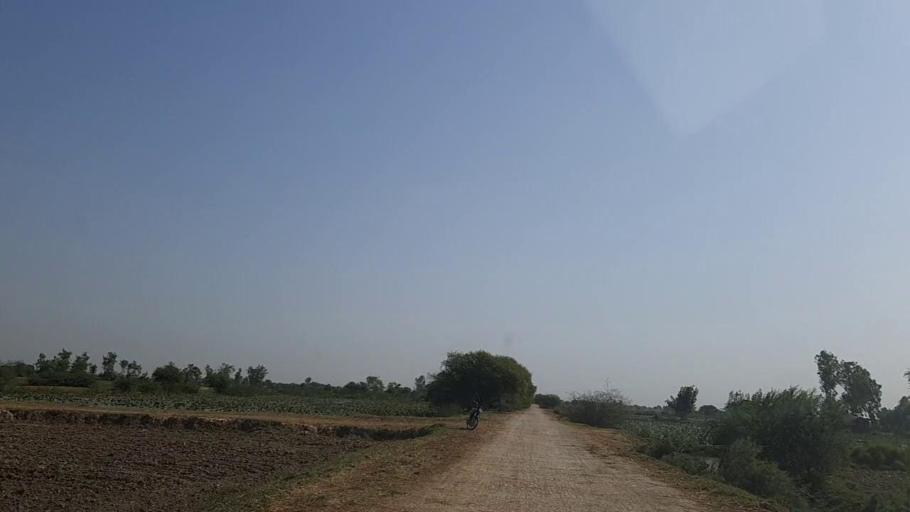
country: PK
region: Sindh
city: Daro Mehar
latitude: 24.7207
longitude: 68.1045
